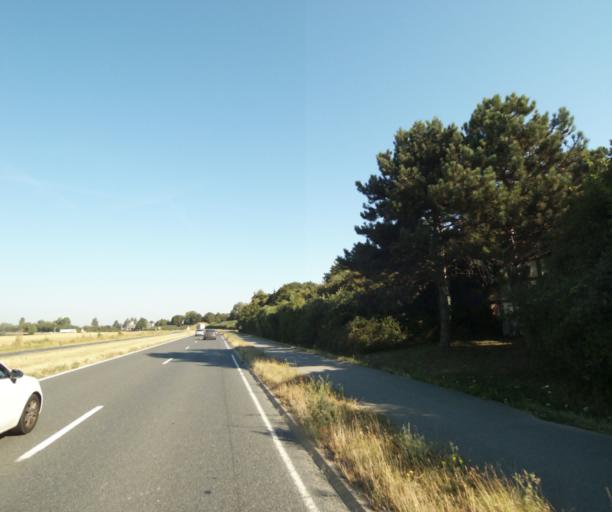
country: FR
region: Ile-de-France
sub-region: Departement de Seine-et-Marne
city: Moissy-Cramayel
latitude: 48.6232
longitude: 2.5797
